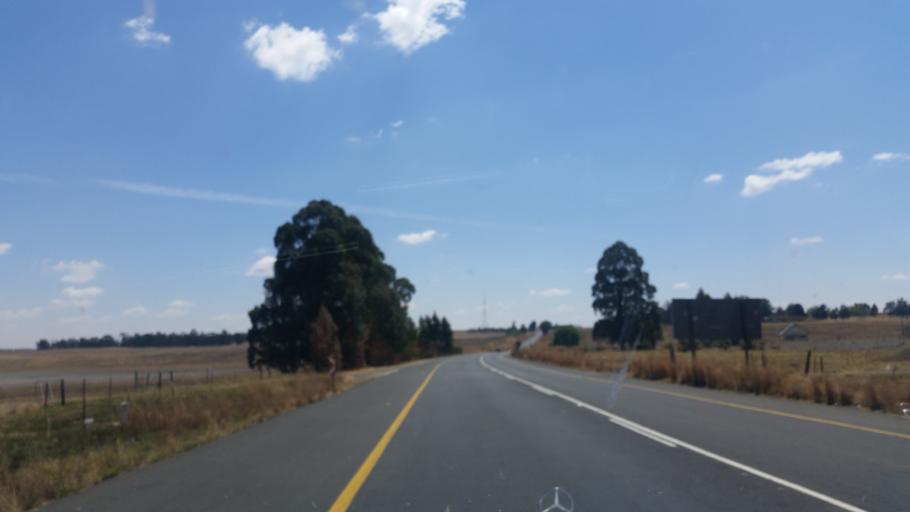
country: ZA
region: Orange Free State
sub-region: Thabo Mofutsanyana District Municipality
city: Reitz
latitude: -28.0813
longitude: 28.6475
